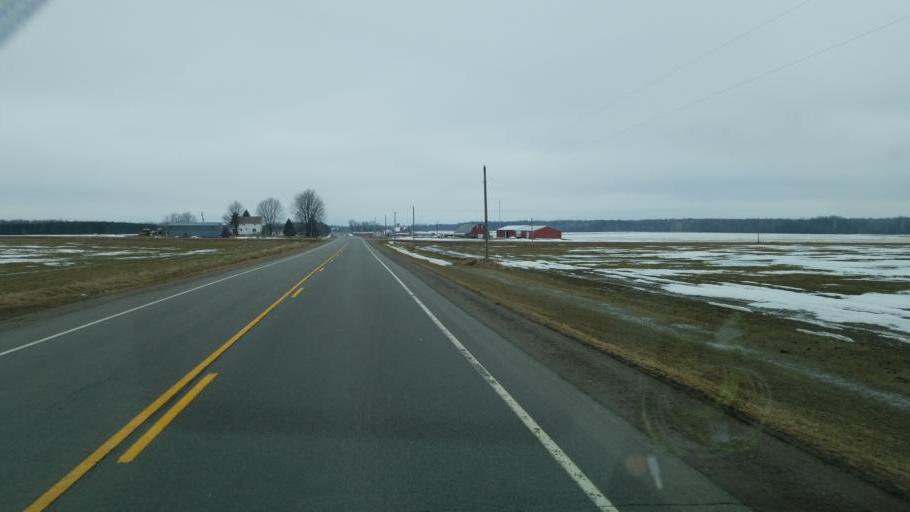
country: US
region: Wisconsin
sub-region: Marathon County
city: Spencer
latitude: 44.6562
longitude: -90.3338
